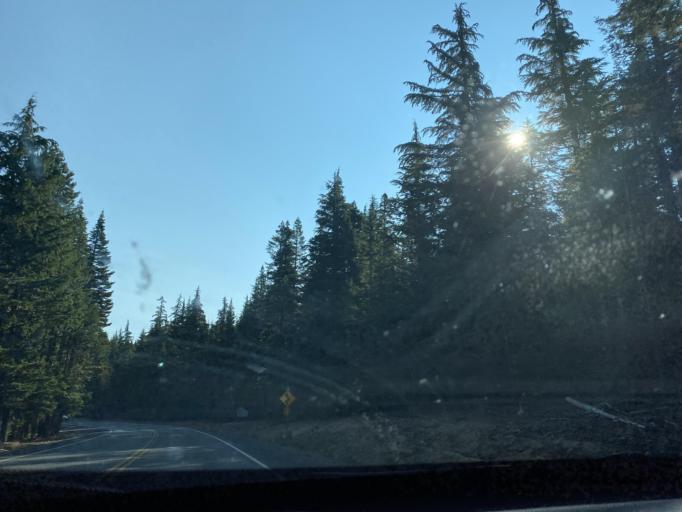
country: US
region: Oregon
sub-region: Deschutes County
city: Three Rivers
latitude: 43.7098
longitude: -121.2840
